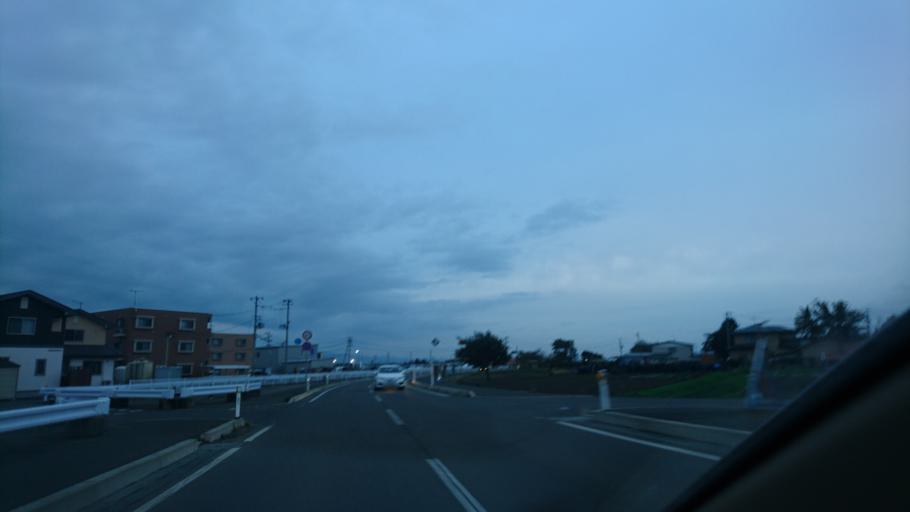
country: JP
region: Iwate
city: Morioka-shi
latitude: 39.6697
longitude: 141.1321
